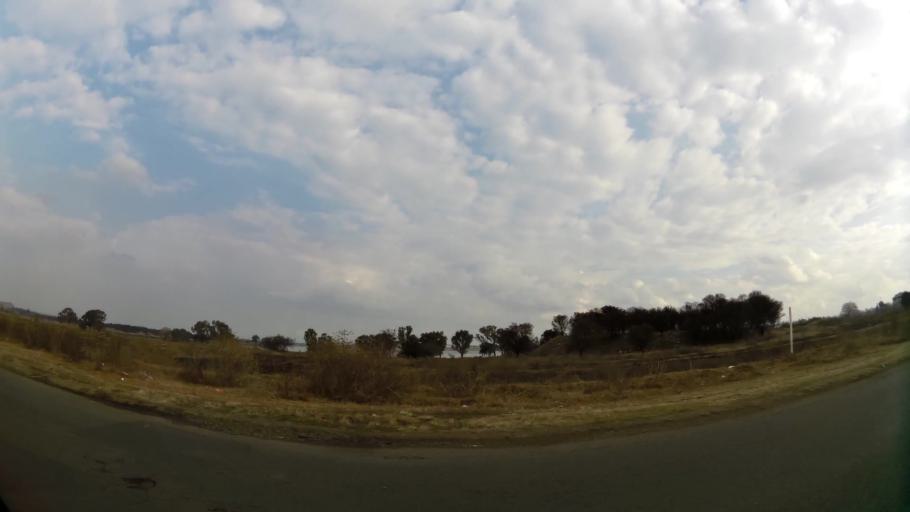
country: ZA
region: Gauteng
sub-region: Sedibeng District Municipality
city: Vereeniging
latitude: -26.6771
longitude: 27.8960
